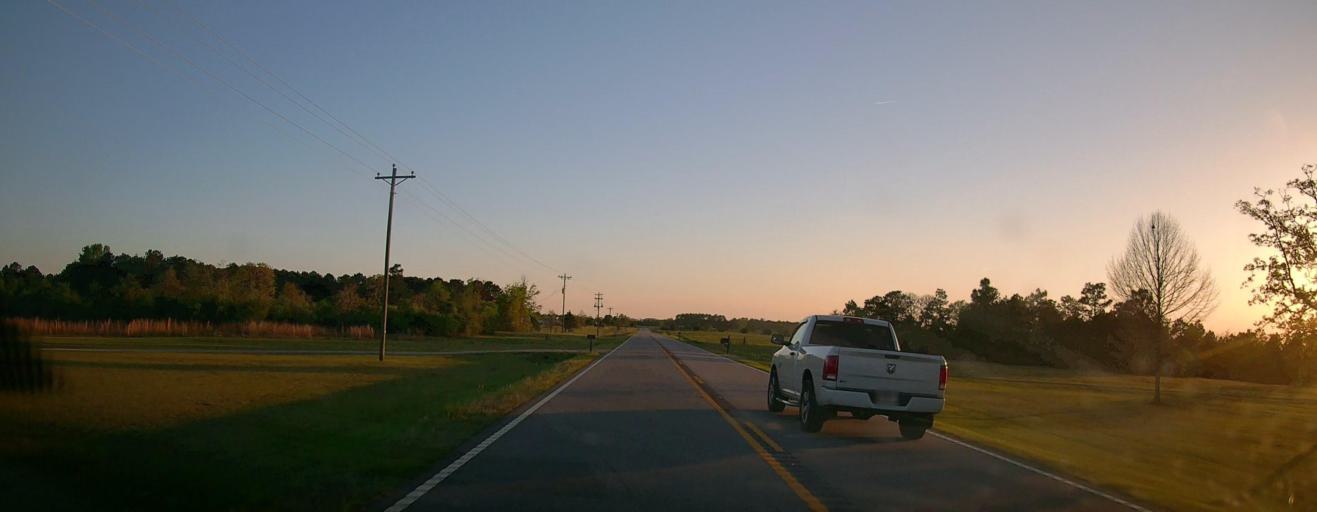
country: US
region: Georgia
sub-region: Marion County
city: Buena Vista
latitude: 32.4912
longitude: -84.6178
